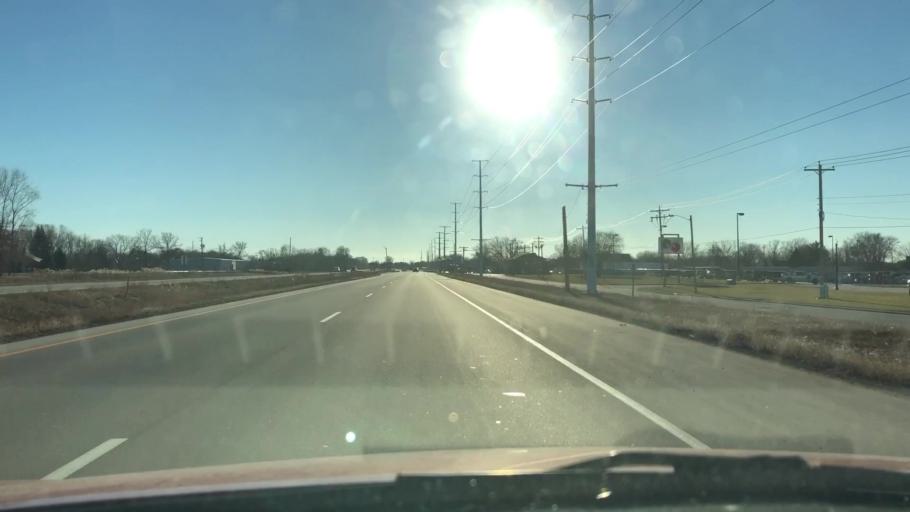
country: US
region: Wisconsin
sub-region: Brown County
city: Ashwaubenon
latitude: 44.4689
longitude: -88.0671
